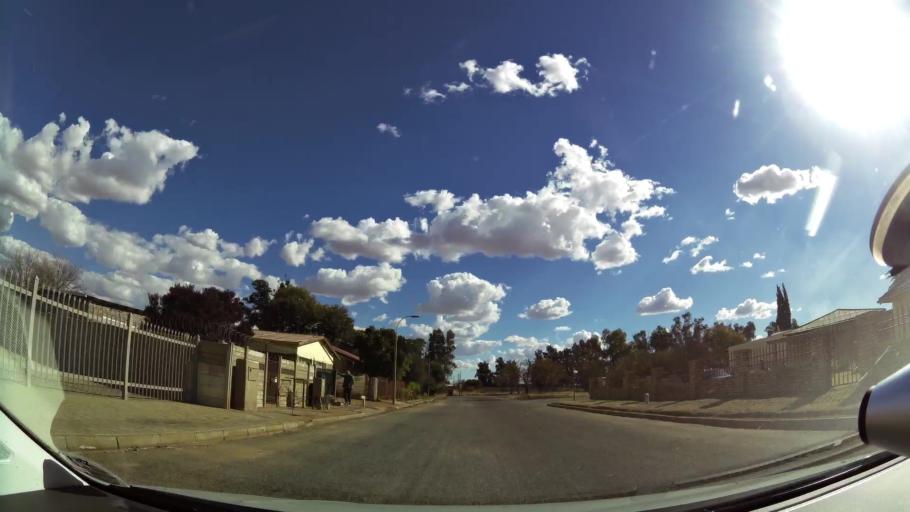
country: ZA
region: North-West
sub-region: Dr Kenneth Kaunda District Municipality
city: Klerksdorp
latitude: -26.8625
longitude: 26.6466
